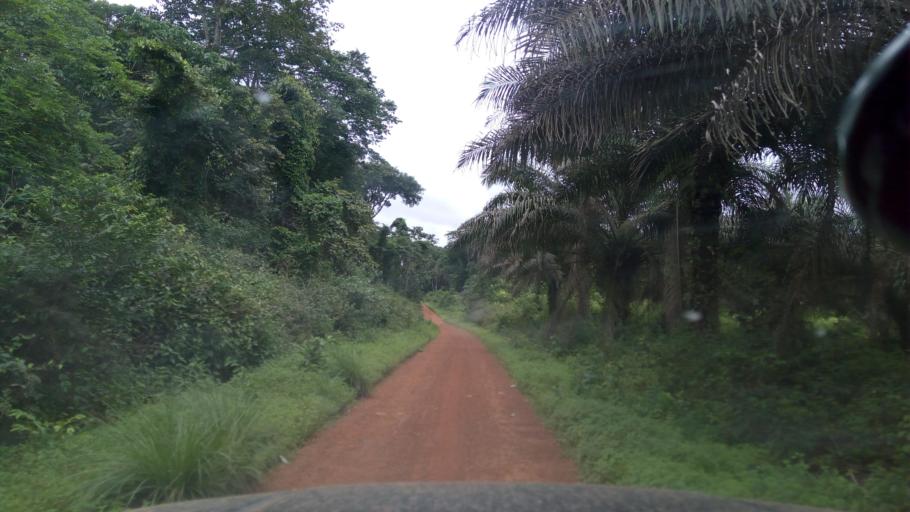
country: SL
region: Eastern Province
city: Gorahun
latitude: 7.6265
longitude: -11.2599
